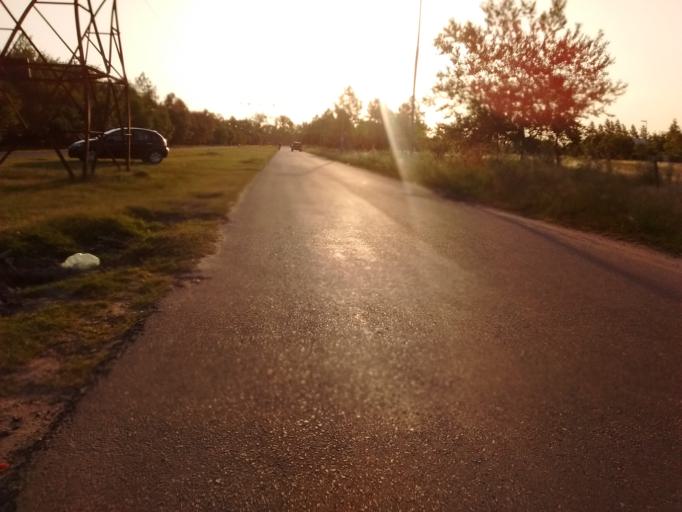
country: AR
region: Santa Fe
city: Funes
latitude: -32.9174
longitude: -60.7604
